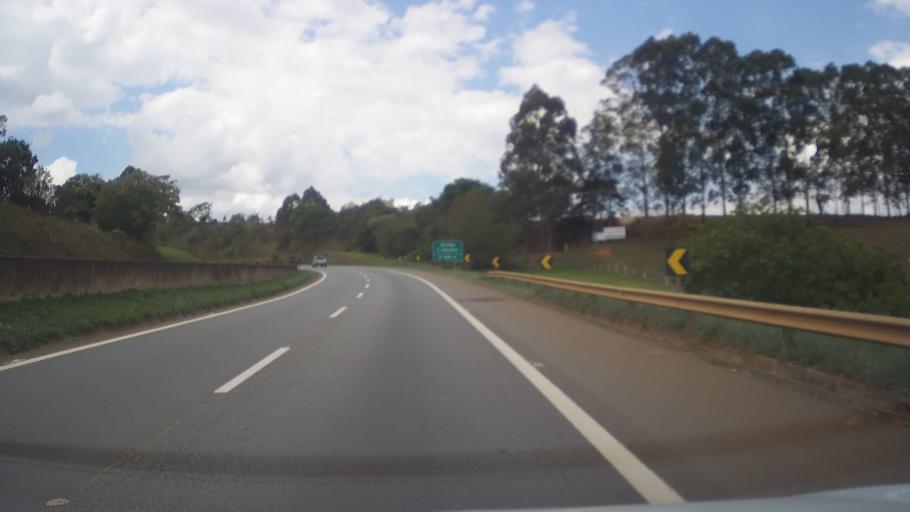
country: BR
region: Minas Gerais
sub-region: Nepomuceno
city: Nepomuceno
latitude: -21.2732
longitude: -45.1366
